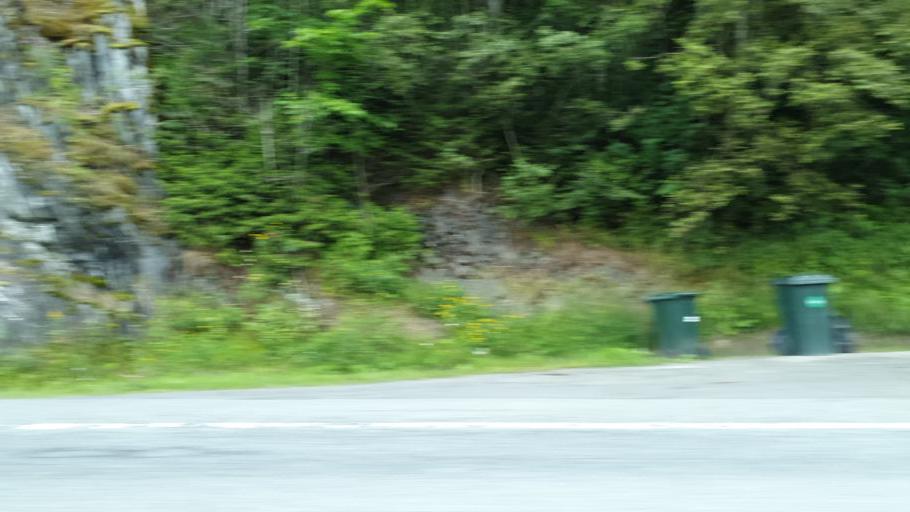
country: NO
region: Sor-Trondelag
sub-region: Midtre Gauldal
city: Storen
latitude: 63.0200
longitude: 10.2472
